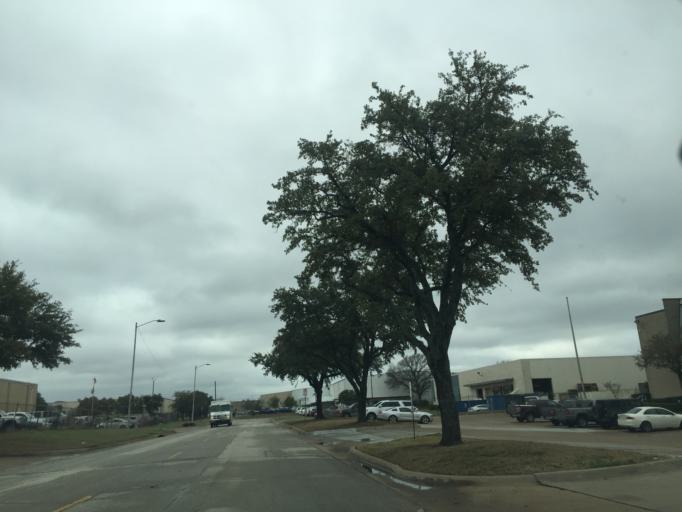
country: US
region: Texas
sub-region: Tarrant County
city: Arlington
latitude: 32.7504
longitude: -97.0574
